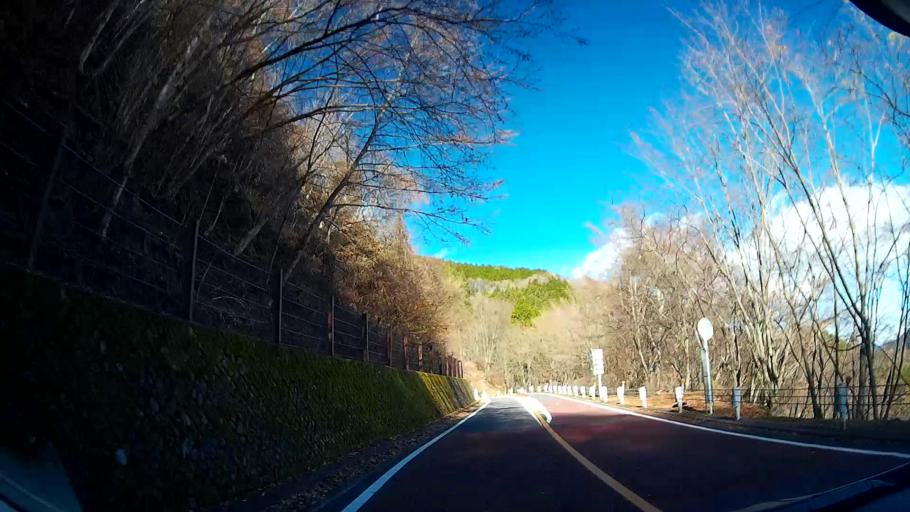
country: JP
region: Yamanashi
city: Uenohara
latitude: 35.7400
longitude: 139.0426
